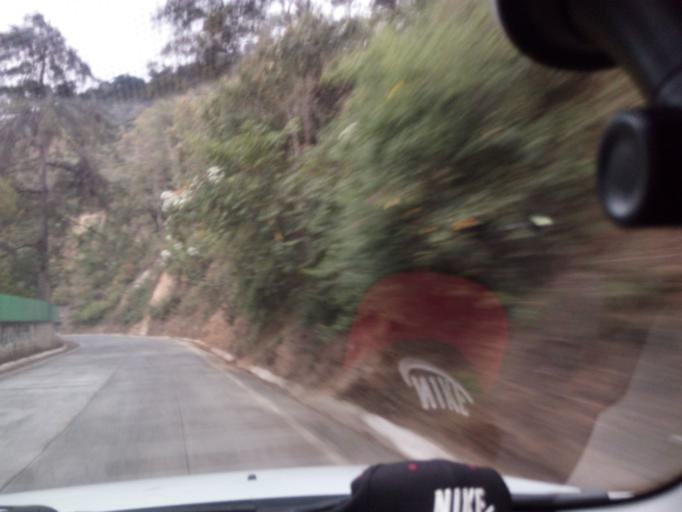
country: GT
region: Sacatepequez
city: Antigua Guatemala
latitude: 14.5709
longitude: -90.7188
